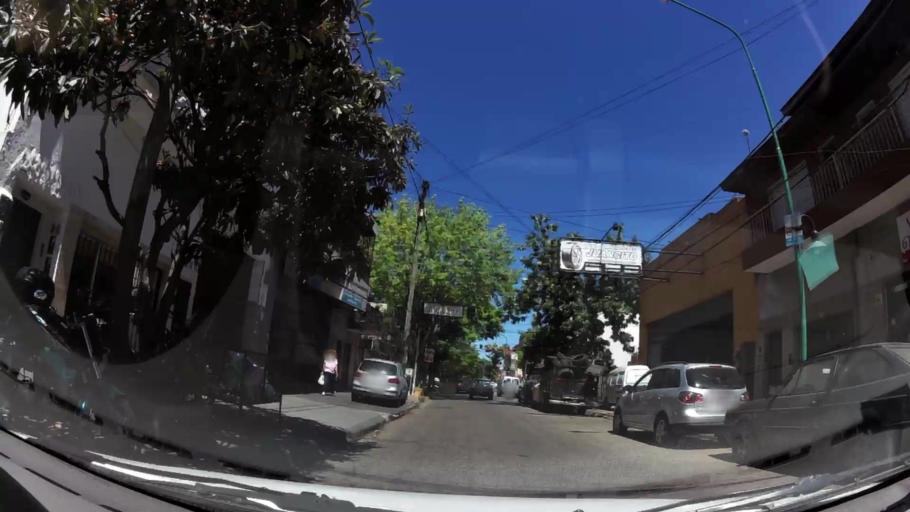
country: AR
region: Buenos Aires
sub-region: Partido de Vicente Lopez
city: Olivos
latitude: -34.5132
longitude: -58.5029
